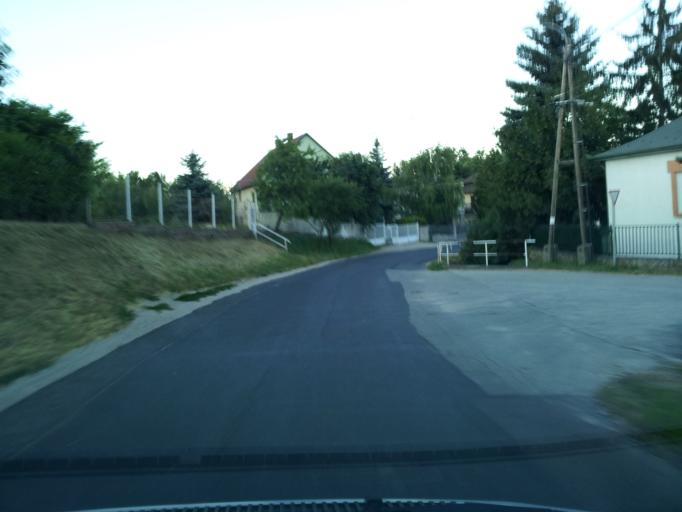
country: HU
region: Veszprem
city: Balatonalmadi
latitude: 47.0220
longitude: 18.0047
